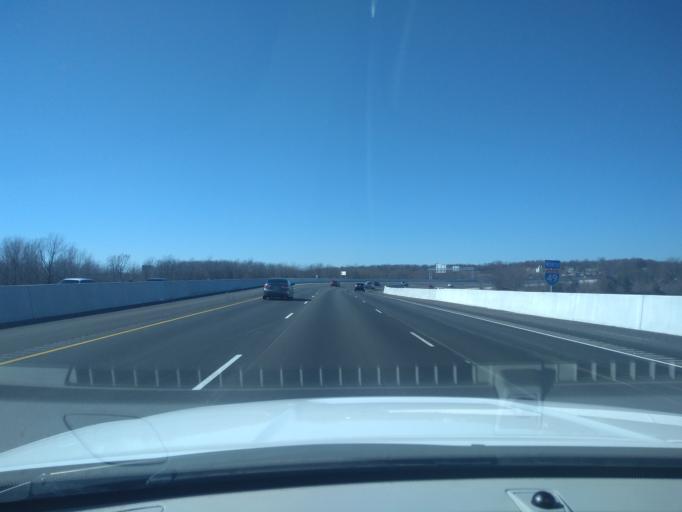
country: US
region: Arkansas
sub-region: Washington County
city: Johnson
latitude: 36.1132
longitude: -94.1730
